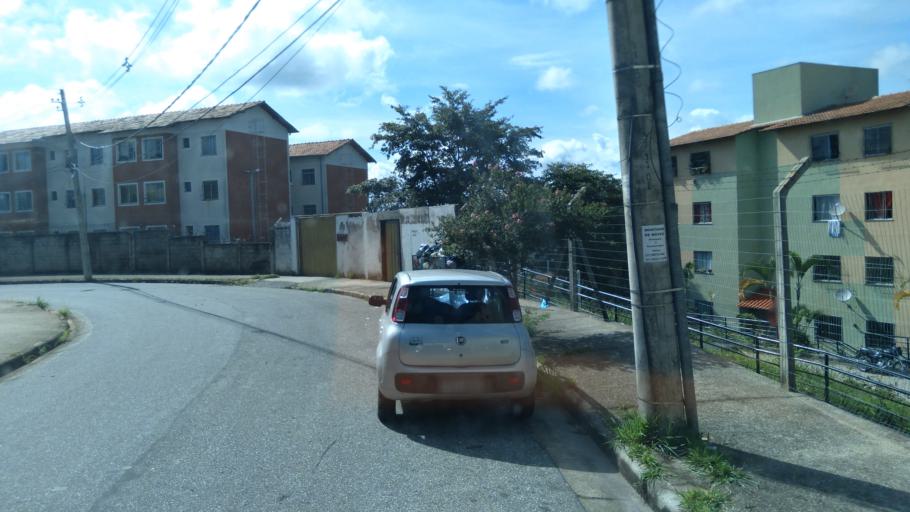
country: BR
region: Minas Gerais
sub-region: Belo Horizonte
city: Belo Horizonte
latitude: -19.8632
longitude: -43.8916
